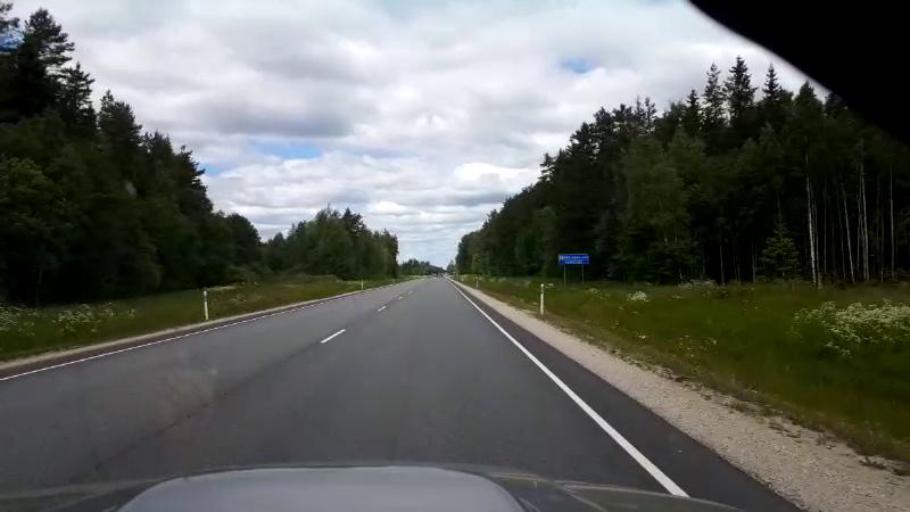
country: EE
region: Raplamaa
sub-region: Maerjamaa vald
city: Marjamaa
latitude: 58.8016
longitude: 24.4128
